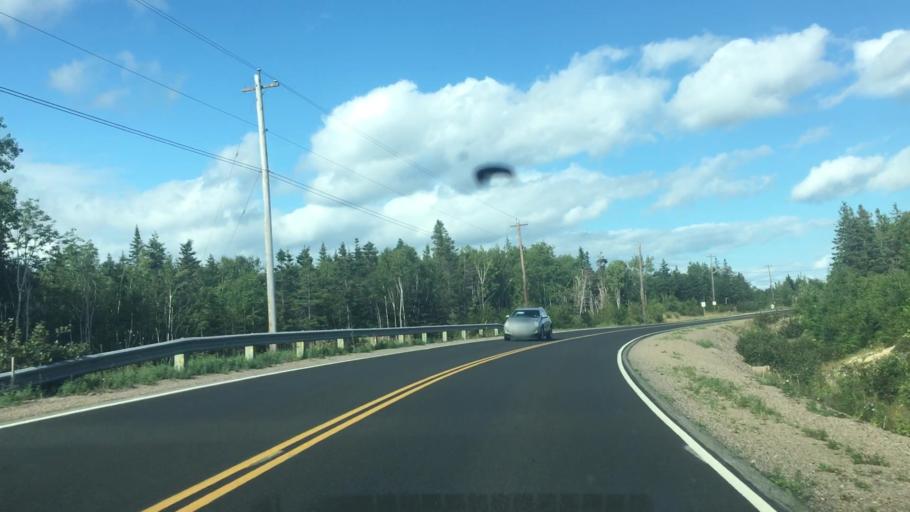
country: CA
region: Nova Scotia
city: Princeville
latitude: 45.8109
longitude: -60.7066
